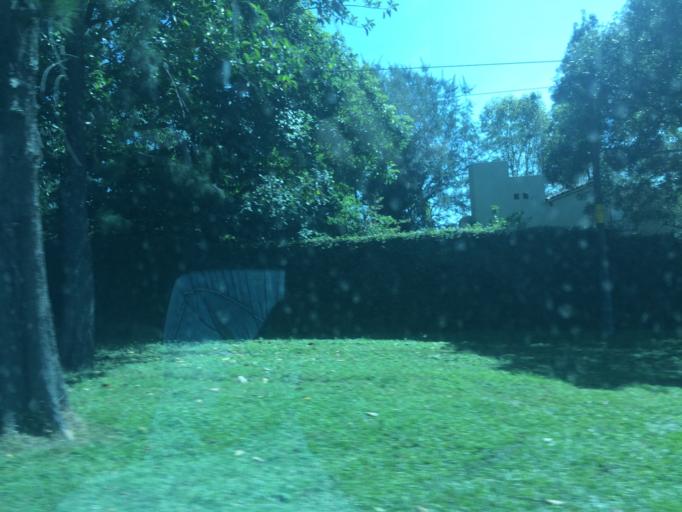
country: MX
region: Colima
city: Suchitlan
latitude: 19.3998
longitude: -103.7012
